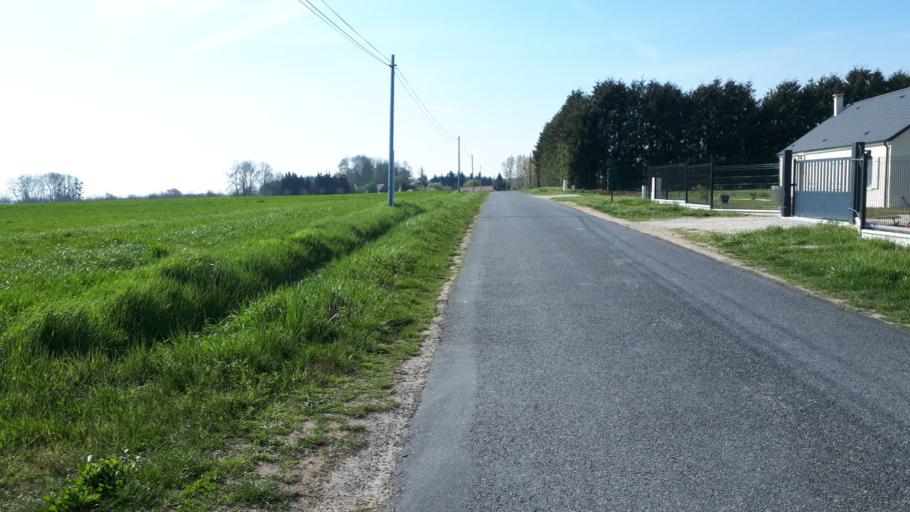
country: FR
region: Centre
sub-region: Departement du Loir-et-Cher
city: Contres
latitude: 47.3868
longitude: 1.3781
